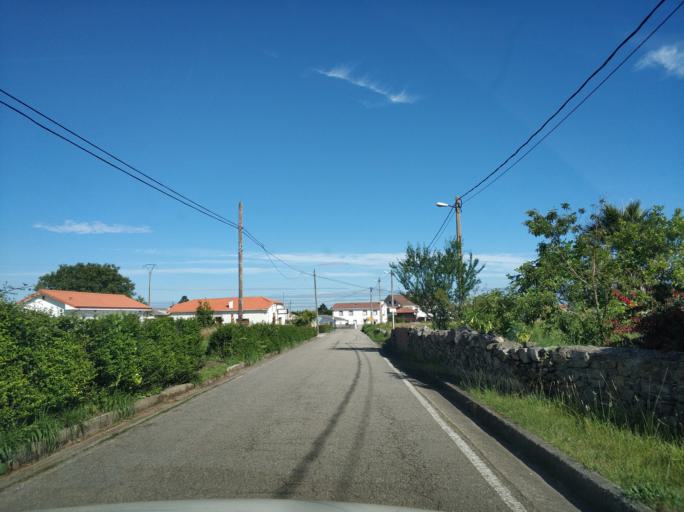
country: ES
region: Asturias
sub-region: Province of Asturias
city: Cudillero
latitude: 43.5727
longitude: -6.2377
